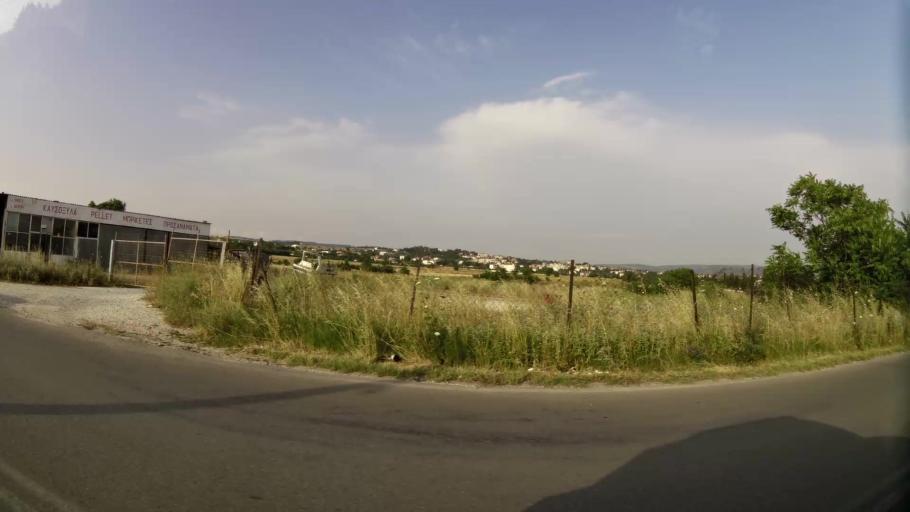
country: GR
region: Central Macedonia
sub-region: Nomos Thessalonikis
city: Oraiokastro
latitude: 40.7103
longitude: 22.9105
